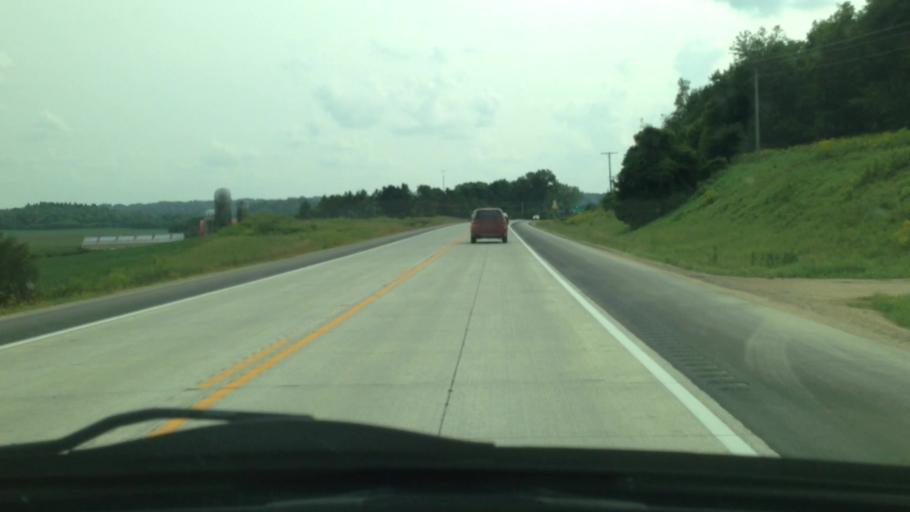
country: US
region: Minnesota
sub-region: Olmsted County
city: Rochester
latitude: 44.1138
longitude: -92.4281
